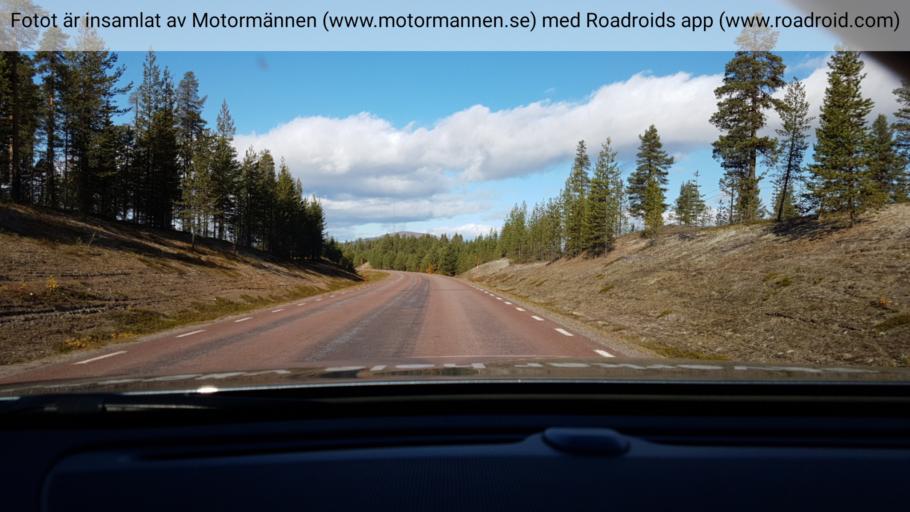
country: SE
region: Norrbotten
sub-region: Arjeplogs Kommun
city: Arjeplog
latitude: 66.0439
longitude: 18.0360
